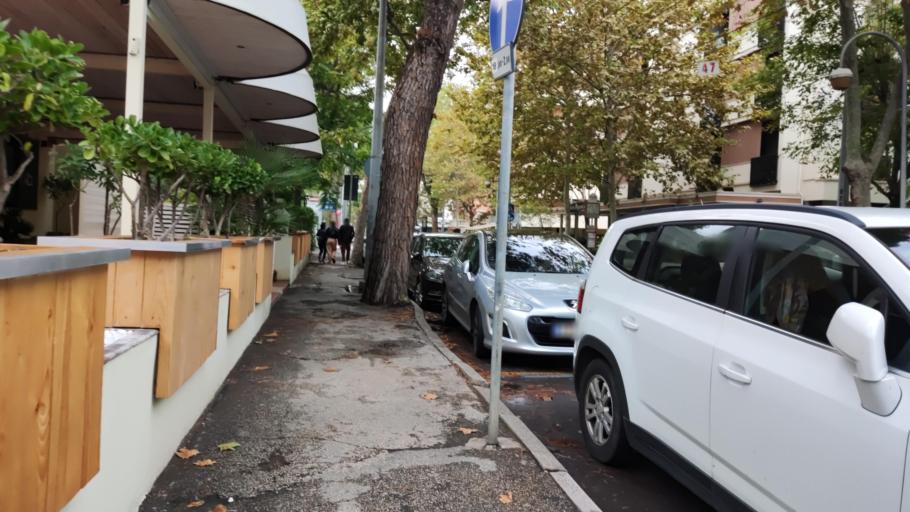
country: IT
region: Emilia-Romagna
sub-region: Provincia di Rimini
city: Riccione
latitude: 44.0070
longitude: 12.6546
